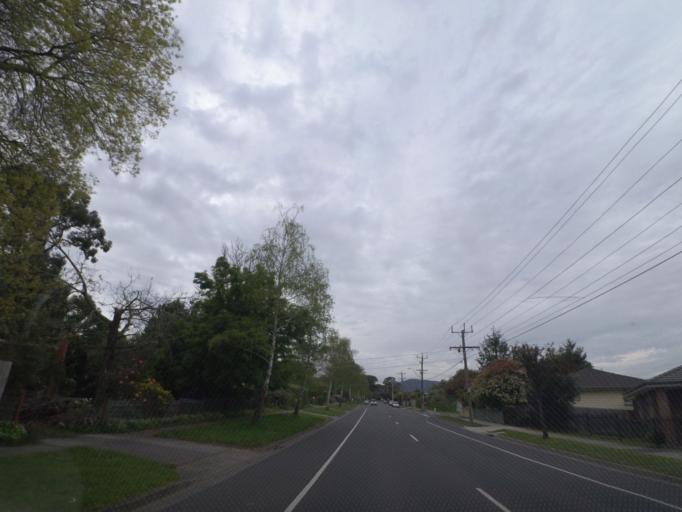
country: AU
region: Victoria
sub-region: Knox
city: The Basin
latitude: -37.8526
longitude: 145.3003
